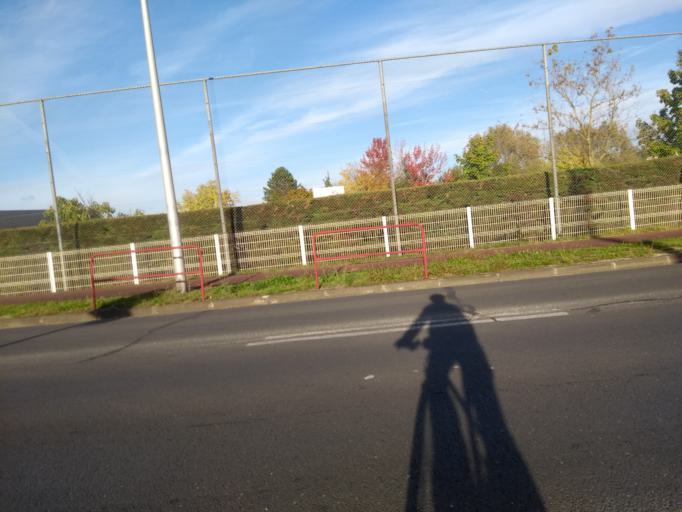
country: FR
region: Aquitaine
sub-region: Departement de la Gironde
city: Pessac
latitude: 44.7980
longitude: -0.6231
